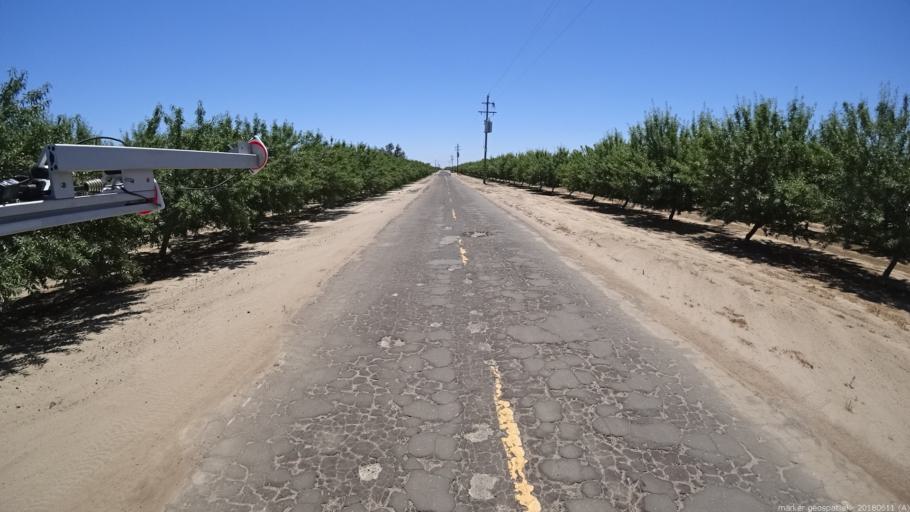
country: US
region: California
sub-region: Madera County
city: Fairmead
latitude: 37.0070
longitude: -120.1933
